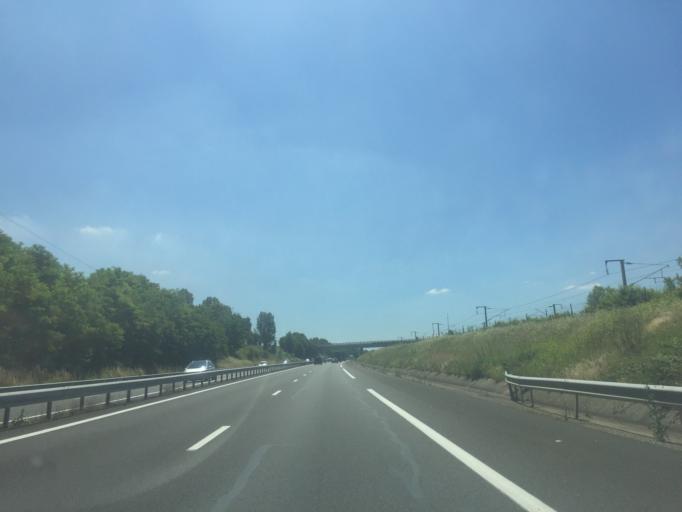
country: FR
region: Rhone-Alpes
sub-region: Departement du Rhone
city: Jons
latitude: 45.8037
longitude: 5.0697
